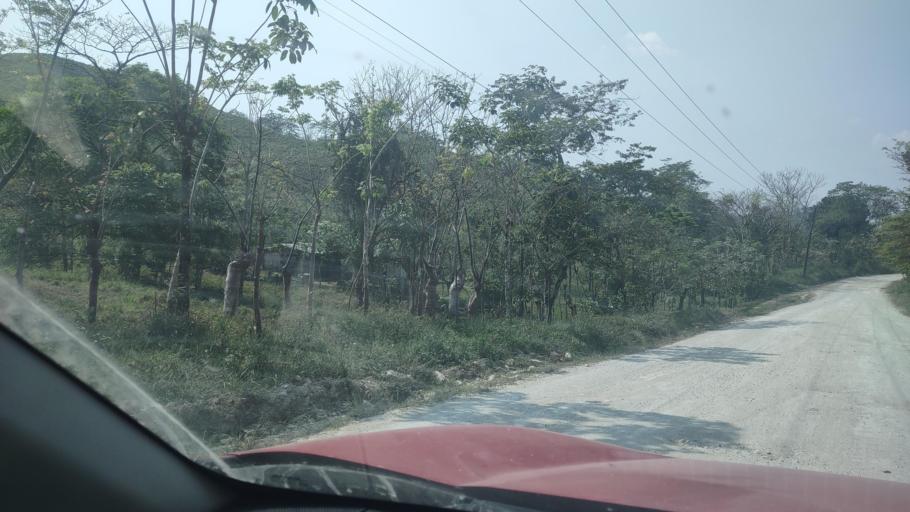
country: MX
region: Tabasco
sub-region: Huimanguillo
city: Francisco Rueda
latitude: 17.5431
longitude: -93.8916
